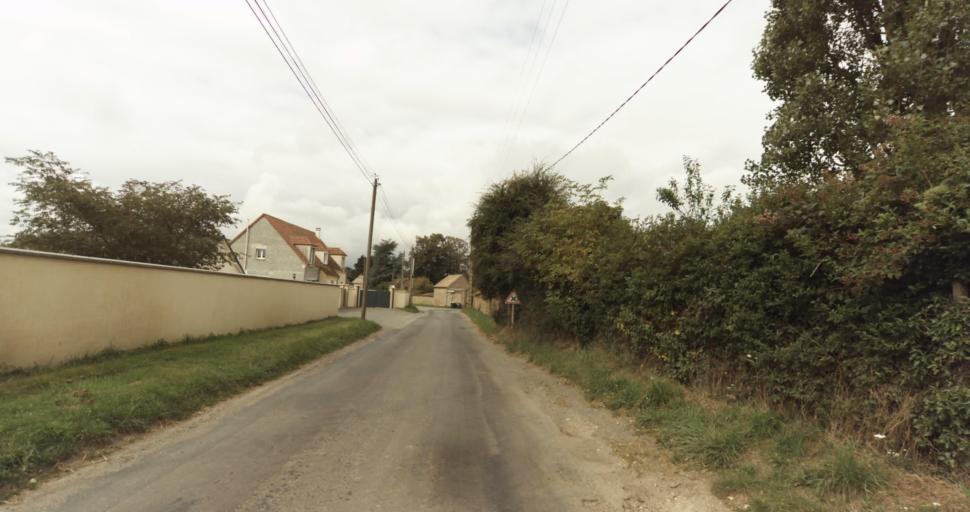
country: FR
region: Haute-Normandie
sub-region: Departement de l'Eure
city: La Couture-Boussey
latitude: 48.9309
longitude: 1.3249
